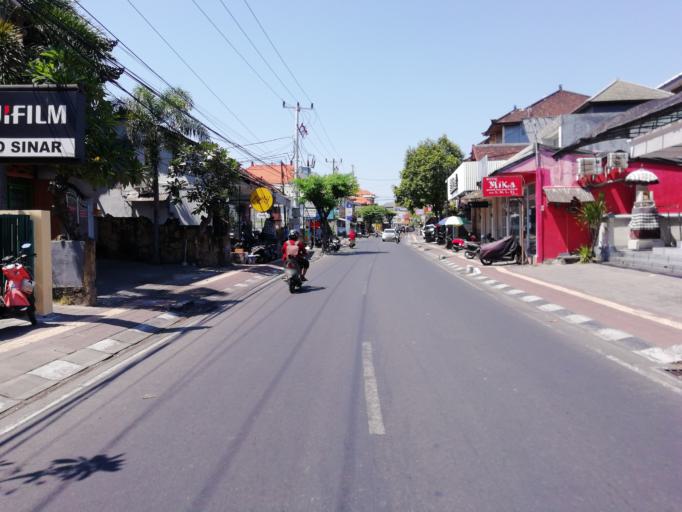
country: ID
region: Bali
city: Karyadharma
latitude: -8.6781
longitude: 115.2238
